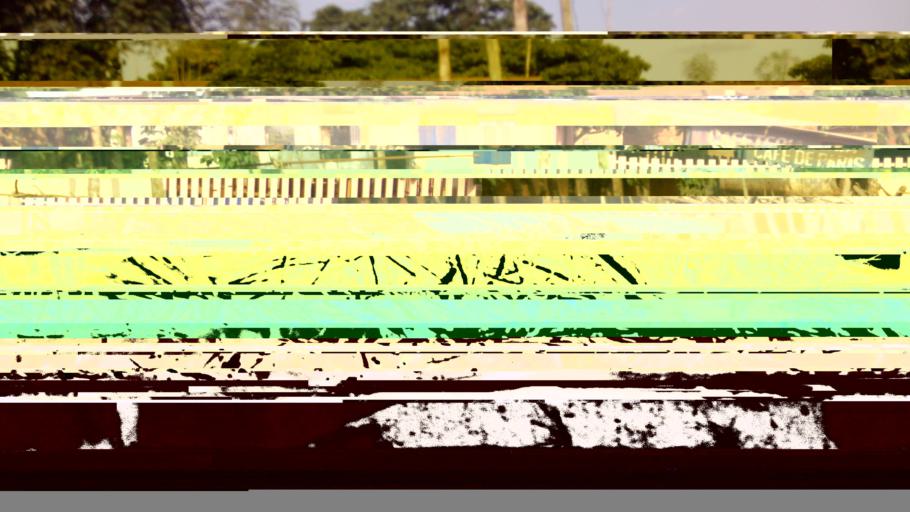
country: TG
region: Maritime
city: Tsevie
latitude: 6.3863
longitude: 1.2024
